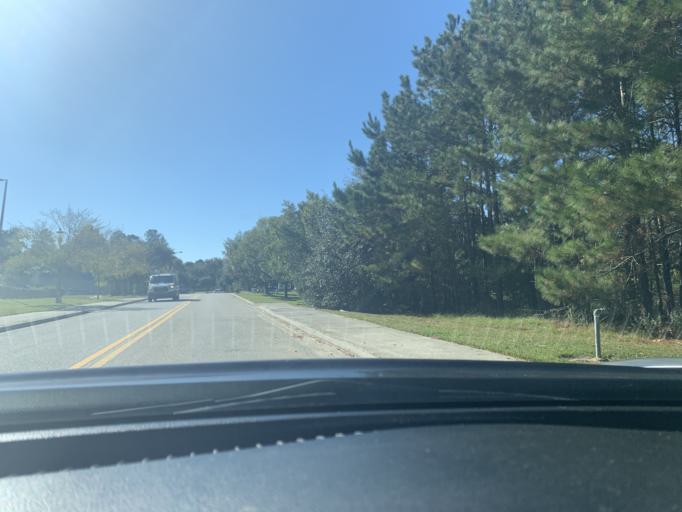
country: US
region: Georgia
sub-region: Chatham County
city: Pooler
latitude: 32.1333
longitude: -81.2573
